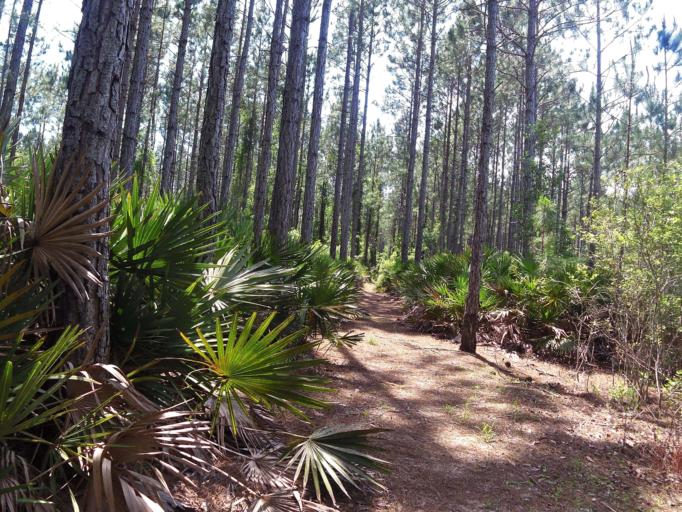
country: US
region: Florida
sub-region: Nassau County
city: Yulee
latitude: 30.4925
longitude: -81.4954
